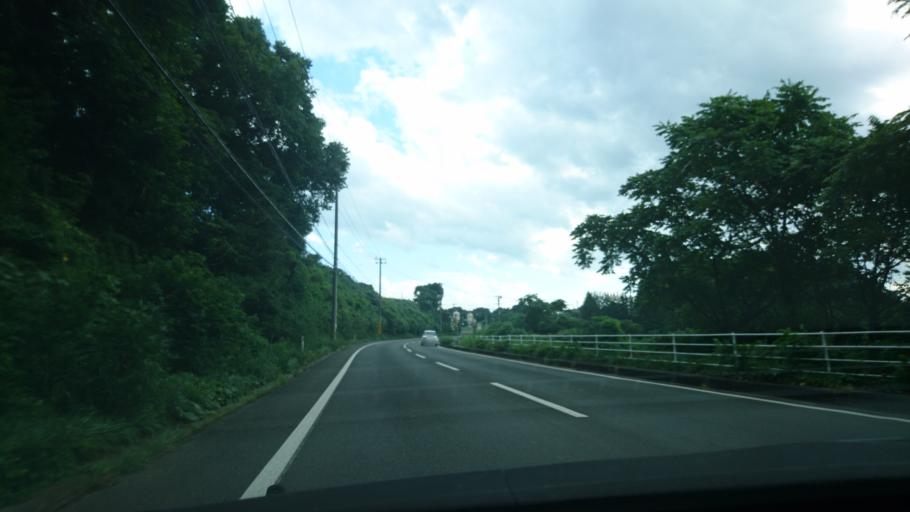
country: JP
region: Iwate
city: Kitakami
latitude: 39.2552
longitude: 141.1222
